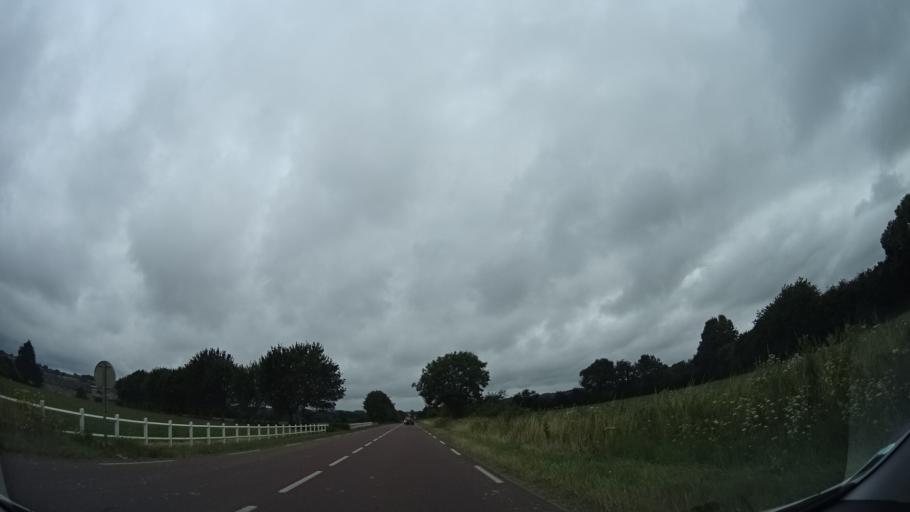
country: FR
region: Lower Normandy
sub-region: Departement de la Manche
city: La Haye-du-Puits
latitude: 49.2674
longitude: -1.5393
